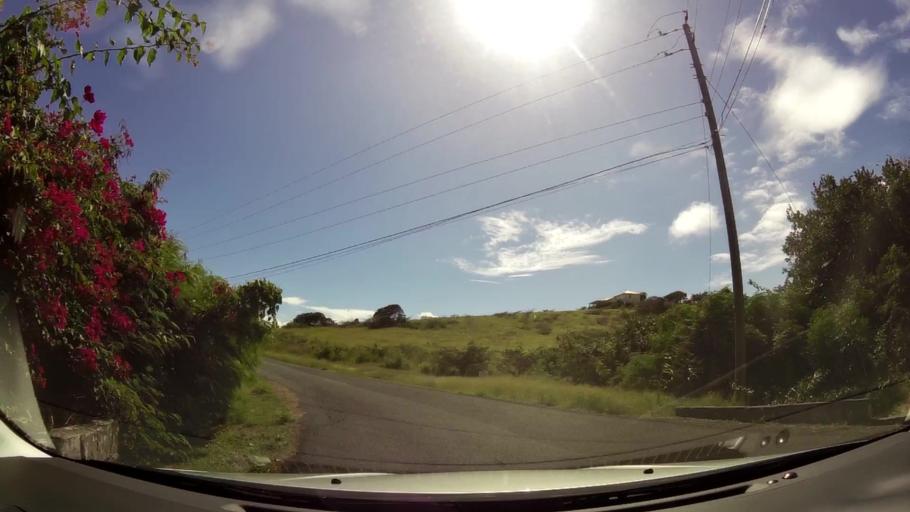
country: AG
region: Saint Paul
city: Falmouth
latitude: 17.0305
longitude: -61.7419
